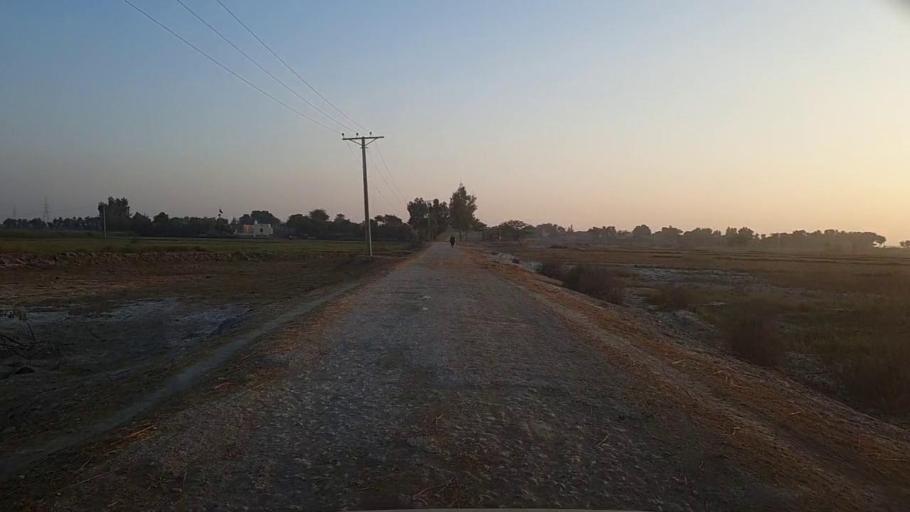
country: PK
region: Sindh
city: Khairpur Nathan Shah
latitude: 27.1605
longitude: 67.7320
